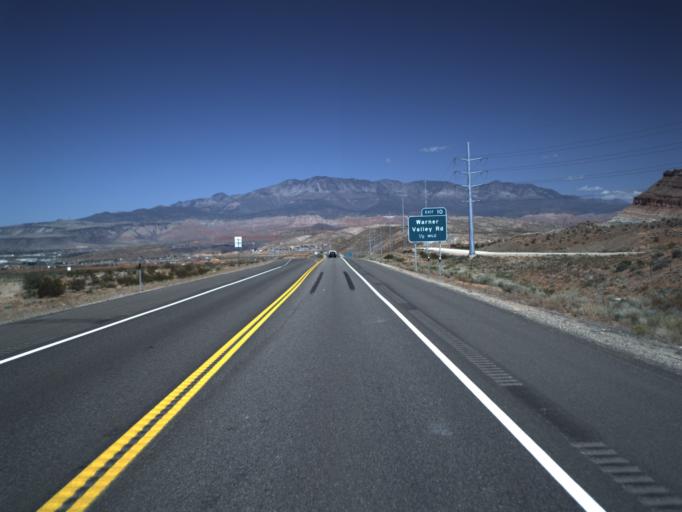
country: US
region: Utah
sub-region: Washington County
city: Washington
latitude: 37.0486
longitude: -113.4857
